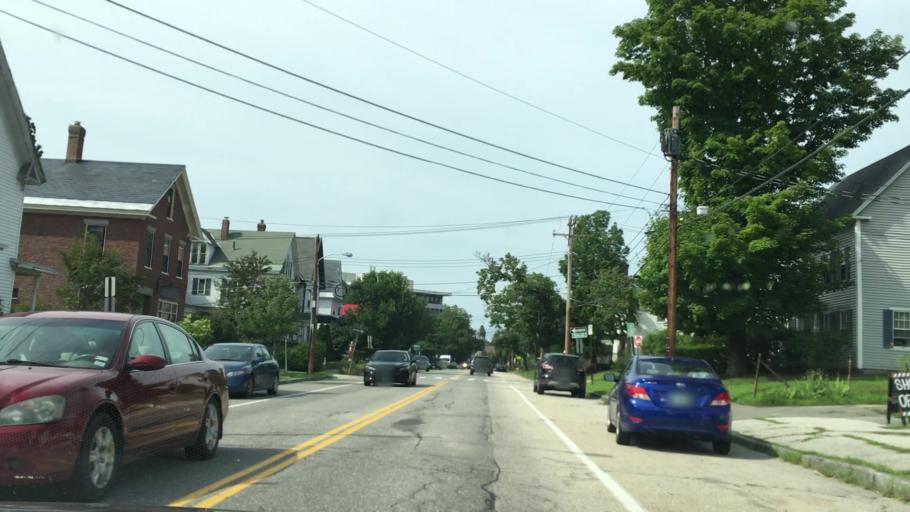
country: US
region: New Hampshire
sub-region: Merrimack County
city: Concord
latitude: 43.1996
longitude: -71.5390
